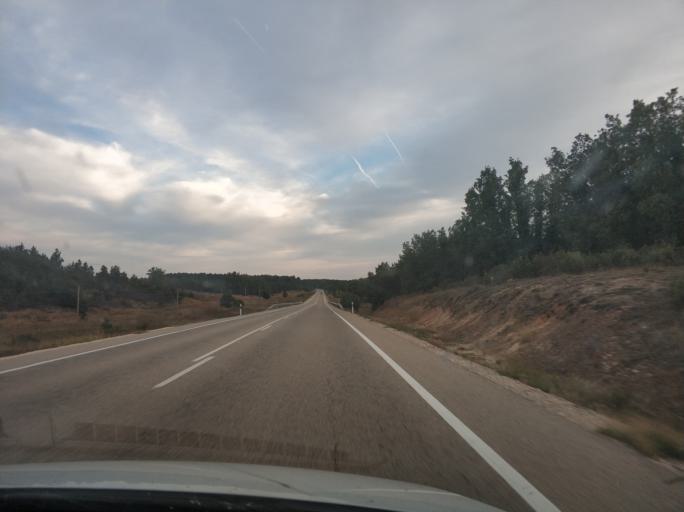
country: ES
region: Castille and Leon
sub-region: Provincia de Burgos
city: Hacinas
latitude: 41.9543
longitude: -3.2914
